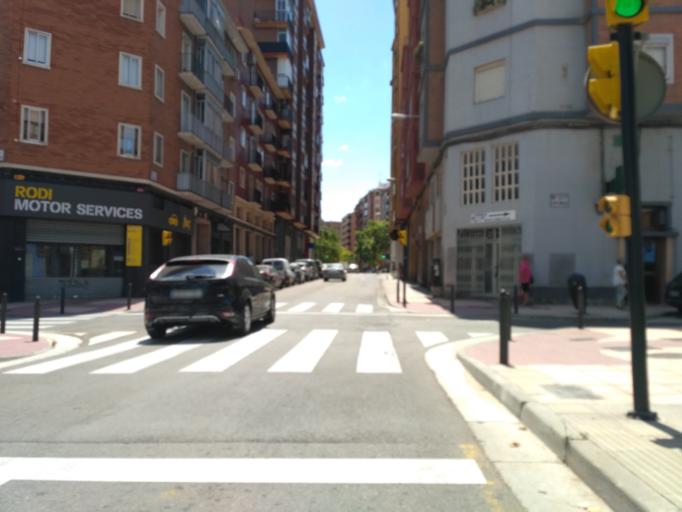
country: ES
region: Aragon
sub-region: Provincia de Zaragoza
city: Almozara
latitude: 41.6561
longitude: -0.9043
